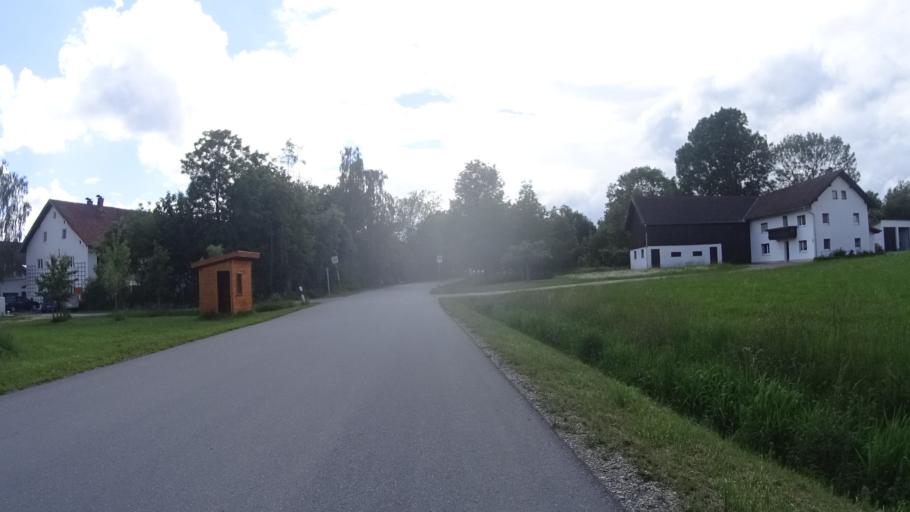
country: DE
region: Bavaria
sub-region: Lower Bavaria
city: Gangkofen
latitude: 48.4479
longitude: 12.5260
